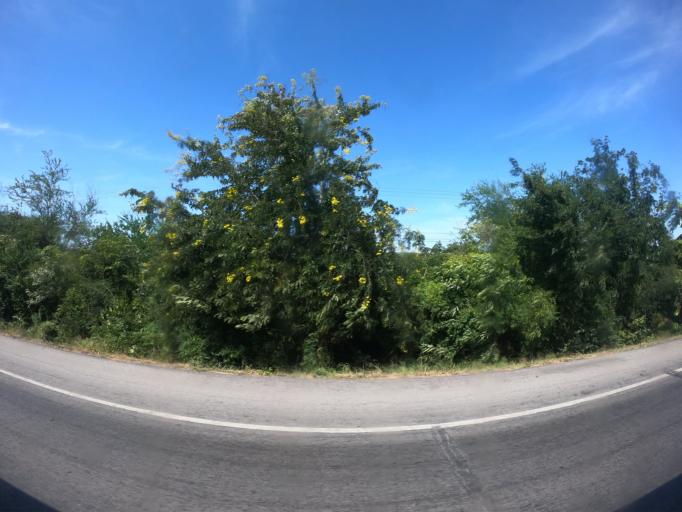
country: TH
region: Nakhon Ratchasima
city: Non Sung
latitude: 15.2028
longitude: 102.3529
